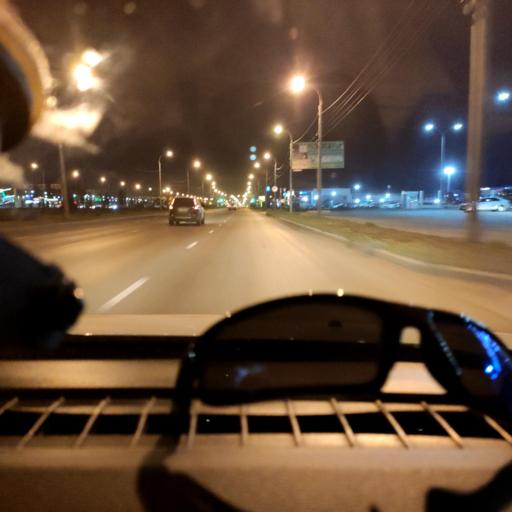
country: RU
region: Samara
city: Samara
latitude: 53.1351
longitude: 50.1750
